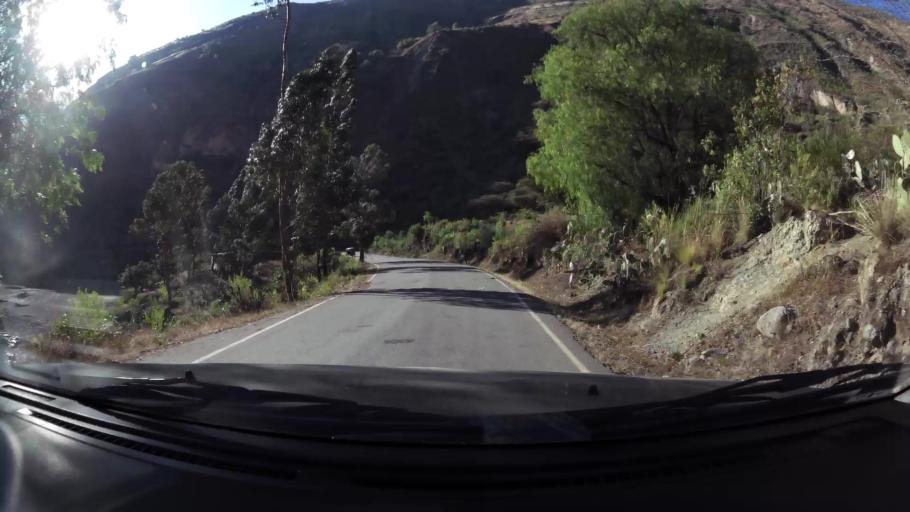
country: PE
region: Huancavelica
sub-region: Provincia de Churcampa
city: La Esmeralda
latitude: -12.5667
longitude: -74.6933
